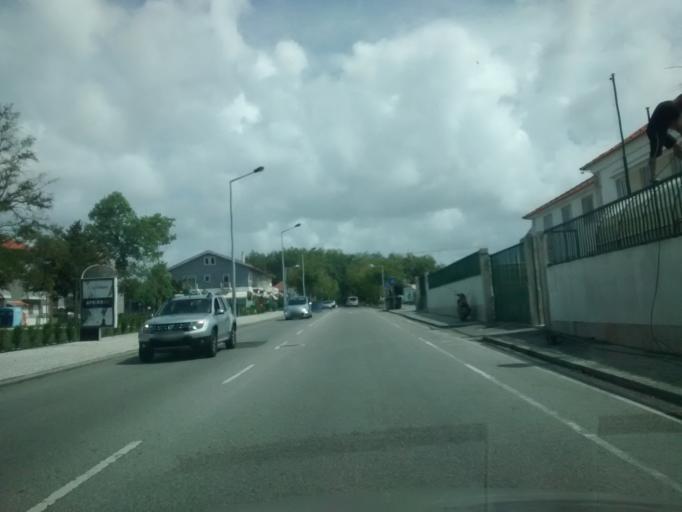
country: PT
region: Aveiro
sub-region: Aveiro
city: Aveiro
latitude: 40.6371
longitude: -8.6574
